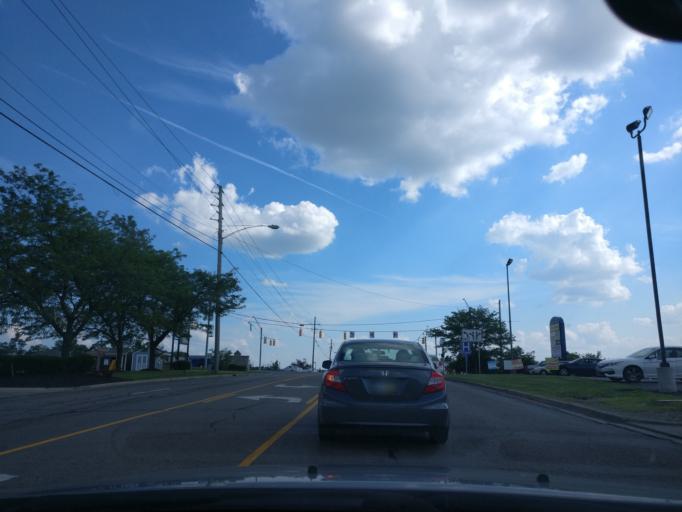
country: US
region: Ohio
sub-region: Montgomery County
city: West Carrollton City
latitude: 39.6416
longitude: -84.2435
